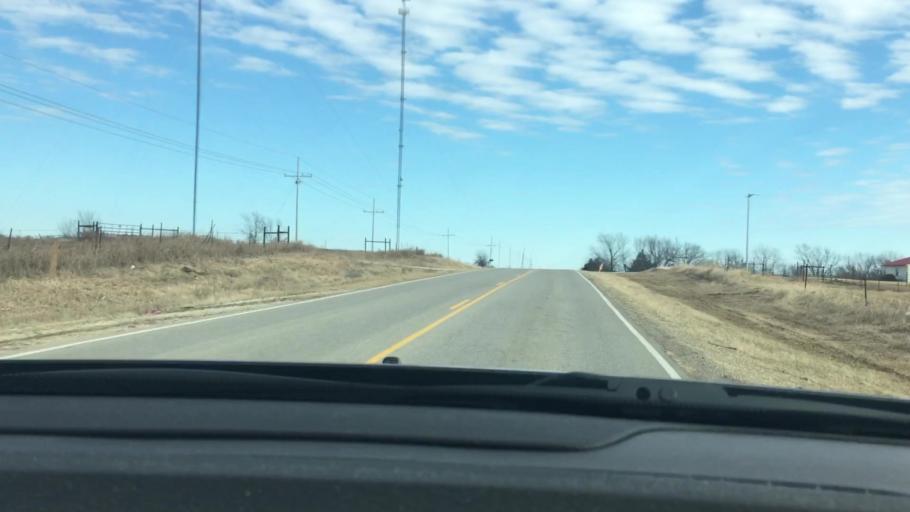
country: US
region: Oklahoma
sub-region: Garvin County
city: Stratford
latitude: 34.7967
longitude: -96.8880
